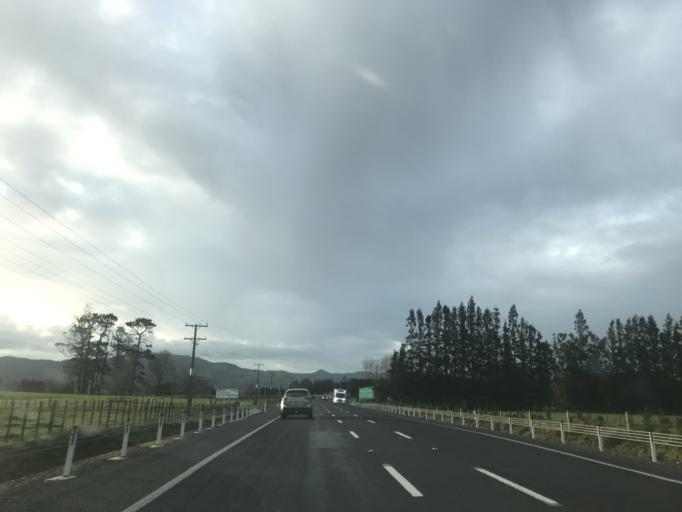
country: NZ
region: Waikato
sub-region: Hauraki District
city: Waihi
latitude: -37.4151
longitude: 175.8647
